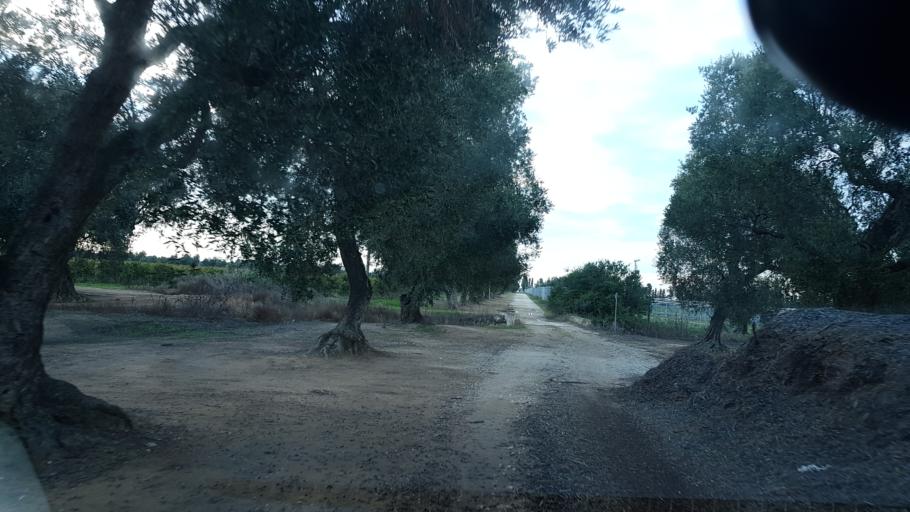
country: IT
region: Apulia
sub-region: Provincia di Brindisi
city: La Rosa
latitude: 40.5911
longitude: 17.9874
